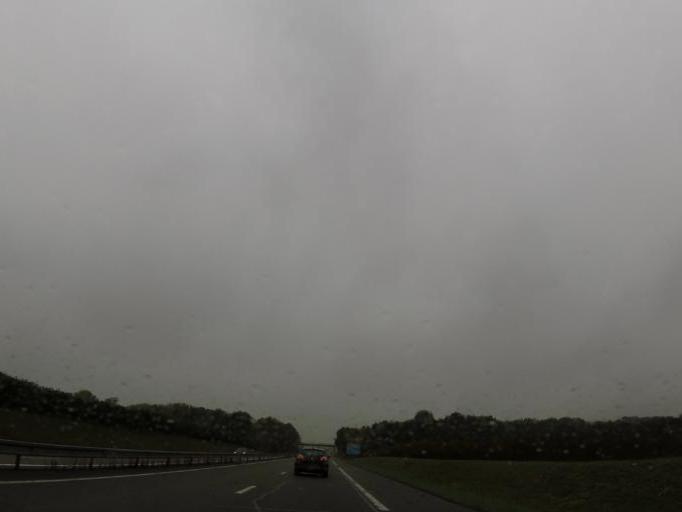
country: FR
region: Champagne-Ardenne
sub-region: Departement de la Marne
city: Saint-Memmie
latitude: 49.0349
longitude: 4.4109
